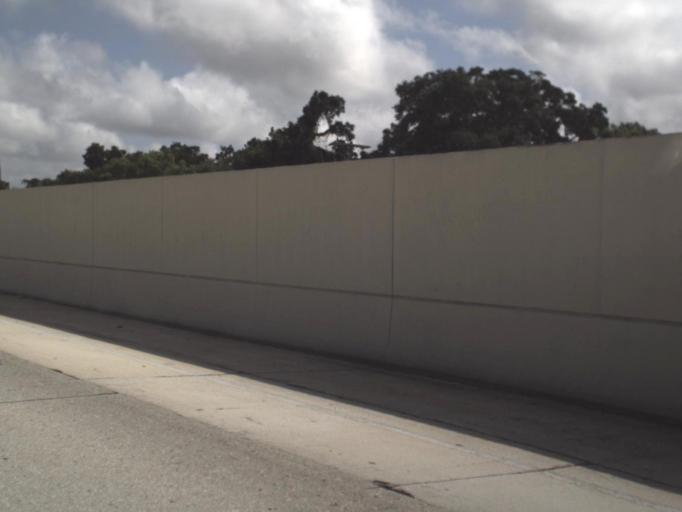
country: US
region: Florida
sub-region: Hillsborough County
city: Tampa
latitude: 27.9695
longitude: -82.4533
